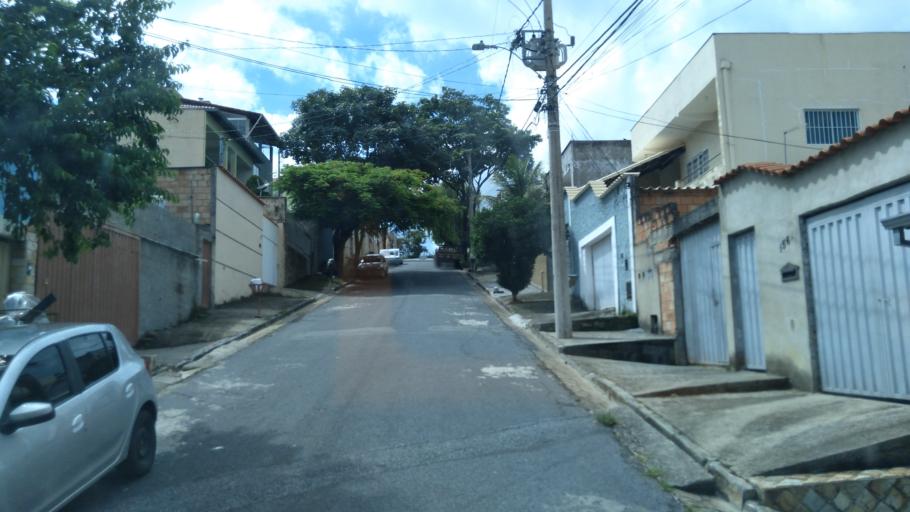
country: BR
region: Minas Gerais
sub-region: Belo Horizonte
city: Belo Horizonte
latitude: -19.8623
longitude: -43.8867
